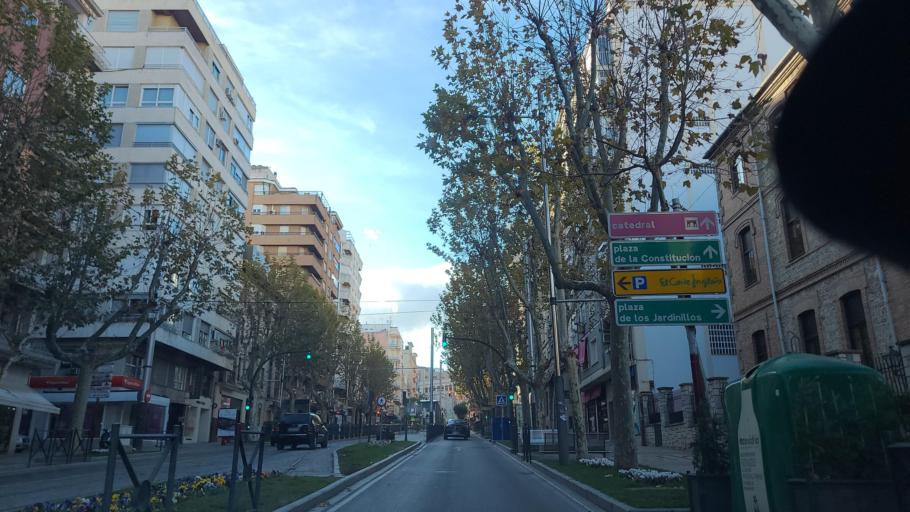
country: ES
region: Andalusia
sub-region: Provincia de Jaen
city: Jaen
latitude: 37.7702
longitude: -3.7884
